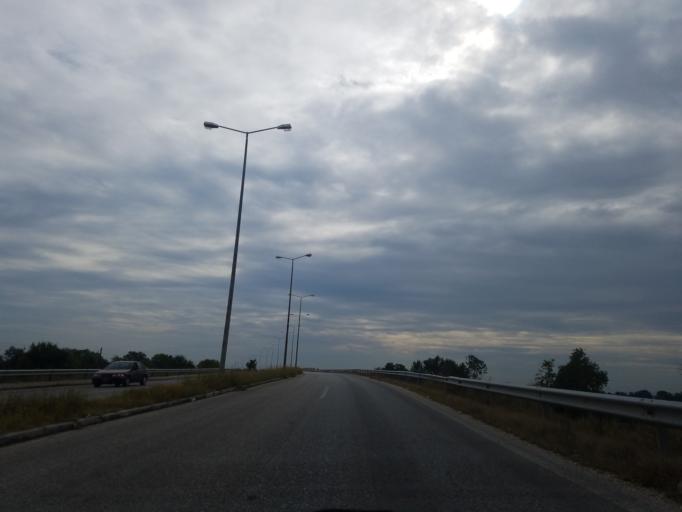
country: GR
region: Thessaly
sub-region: Trikala
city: Pyrgetos
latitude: 39.5212
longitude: 21.7547
